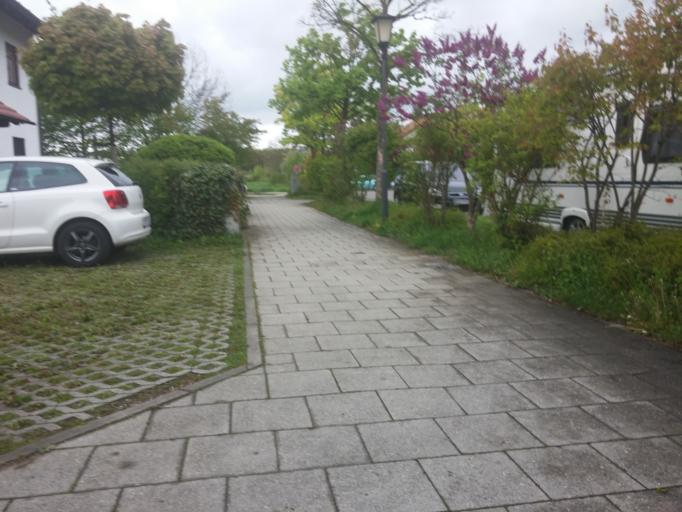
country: DE
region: Bavaria
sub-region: Upper Bavaria
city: Aschheim
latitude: 48.1687
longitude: 11.7097
